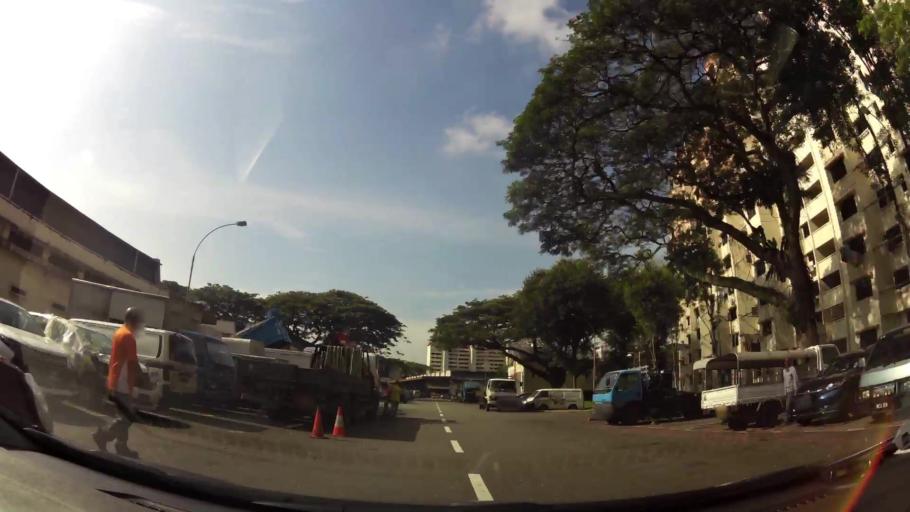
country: SG
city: Singapore
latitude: 1.3571
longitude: 103.8397
